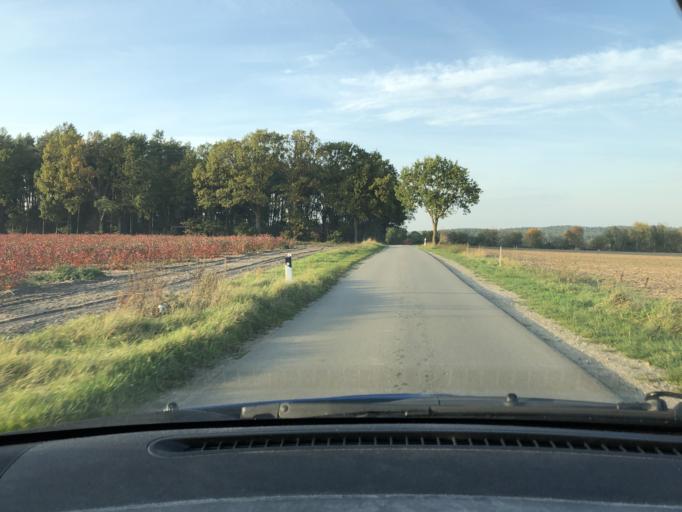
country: DE
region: Lower Saxony
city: Hitzacker
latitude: 53.1400
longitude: 11.0069
